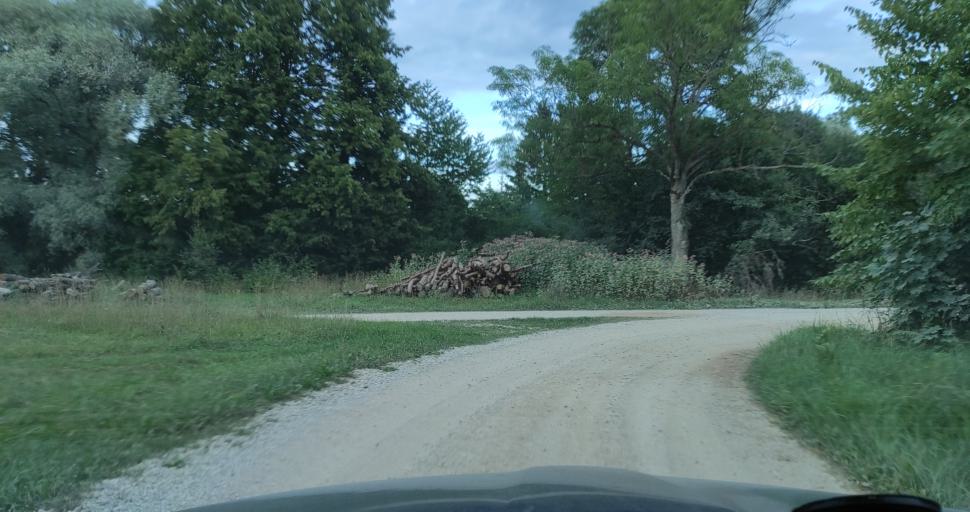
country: LV
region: Alsunga
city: Alsunga
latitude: 56.9349
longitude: 21.6374
